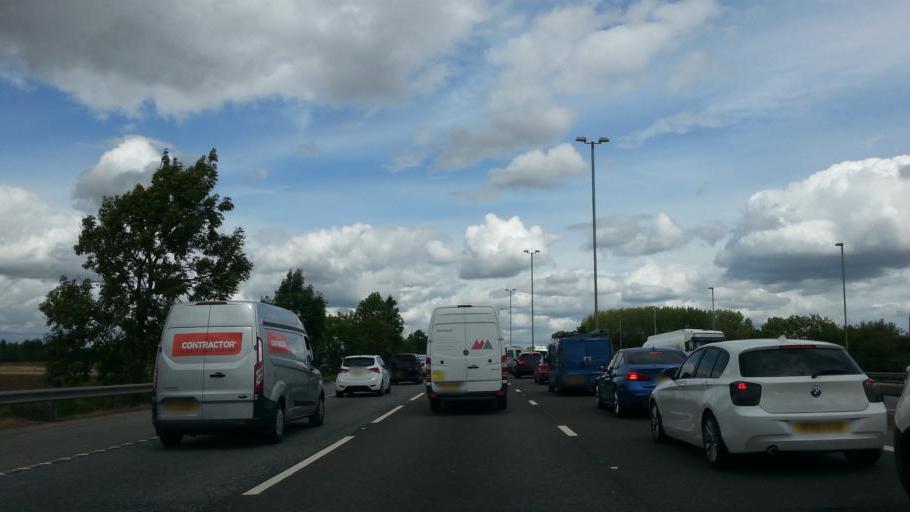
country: GB
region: England
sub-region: Essex
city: Little Hallingbury
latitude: 51.8597
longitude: 0.1890
